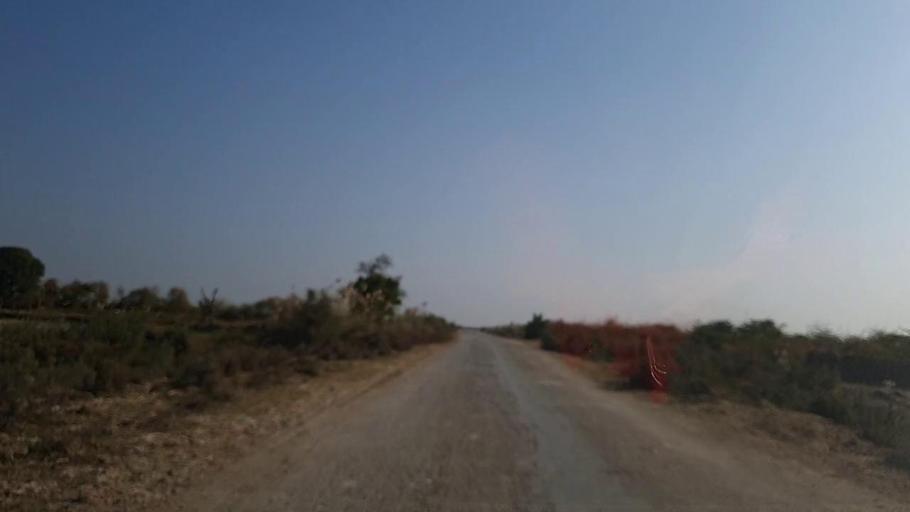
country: PK
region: Sindh
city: Tando Mittha Khan
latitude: 25.9226
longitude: 69.0689
